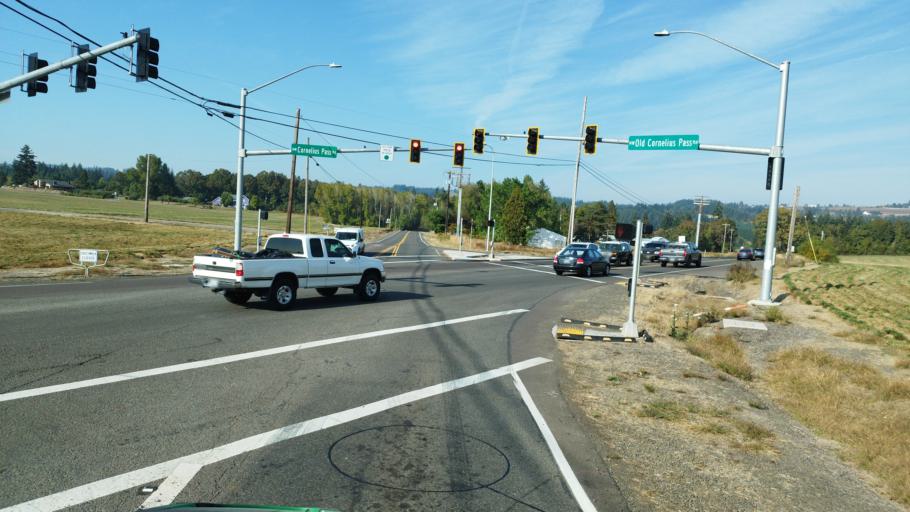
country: US
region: Oregon
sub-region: Washington County
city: Bethany
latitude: 45.5815
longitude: -122.8729
